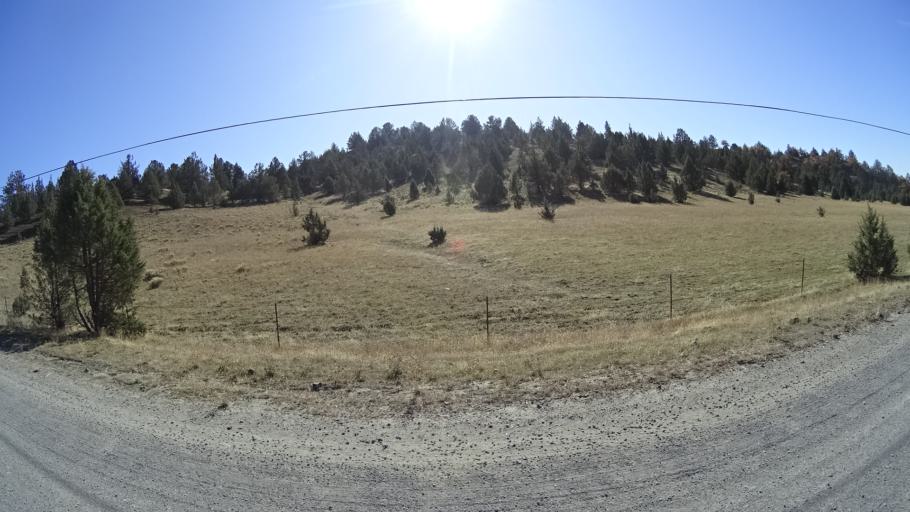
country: US
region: California
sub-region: Siskiyou County
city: Montague
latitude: 41.8083
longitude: -122.3753
